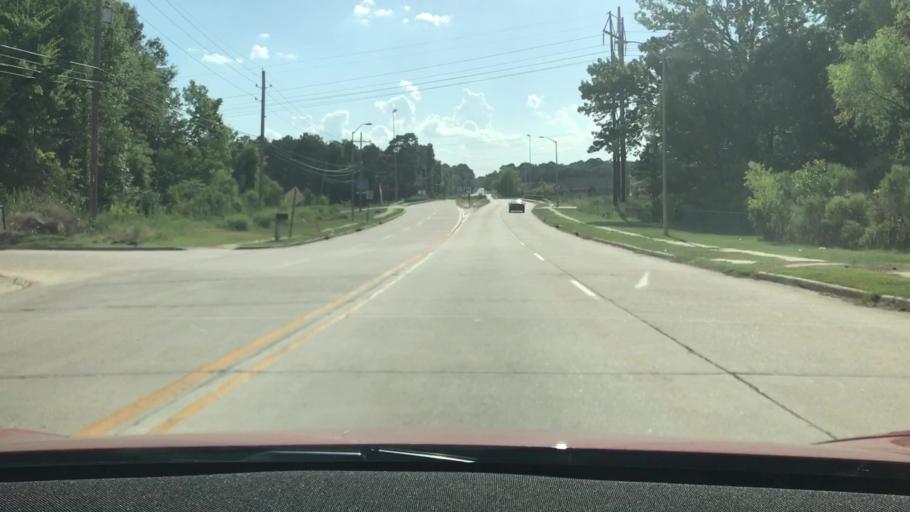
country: US
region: Louisiana
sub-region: Bossier Parish
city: Bossier City
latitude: 32.4130
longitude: -93.7721
